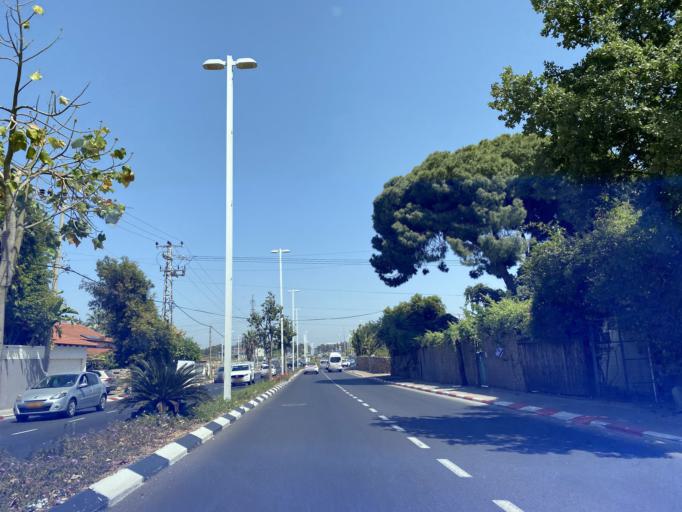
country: IL
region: Tel Aviv
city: Kefar Shemaryahu
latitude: 32.1794
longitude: 34.8204
